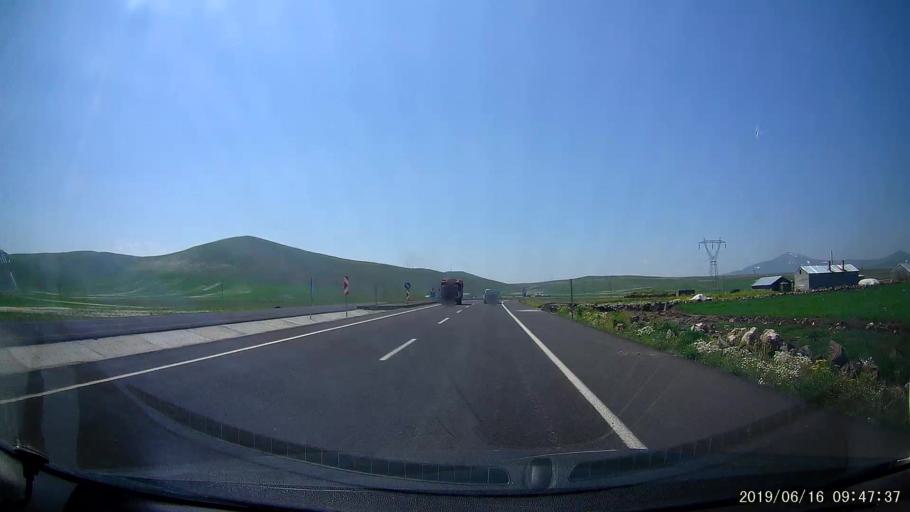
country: TR
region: Kars
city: Digor
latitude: 40.4441
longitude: 43.3460
